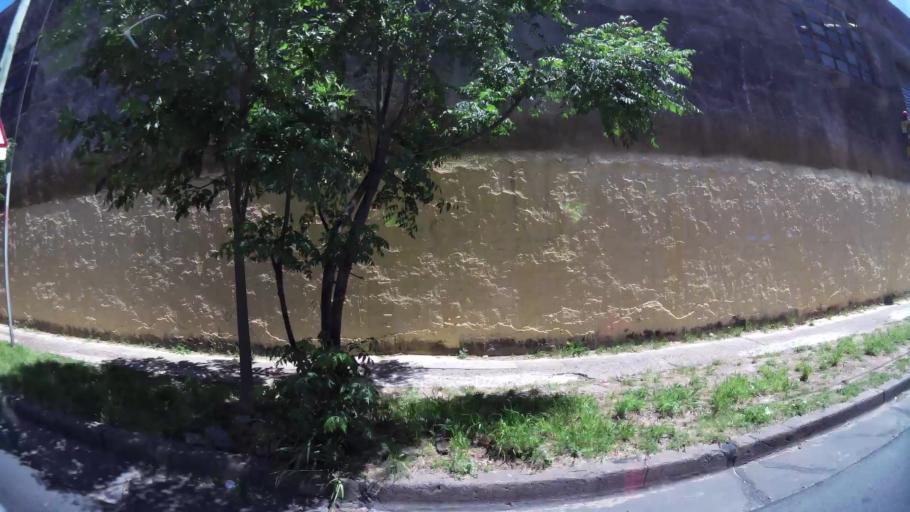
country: AR
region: Buenos Aires
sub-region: Partido de San Isidro
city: San Isidro
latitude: -34.5030
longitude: -58.5481
